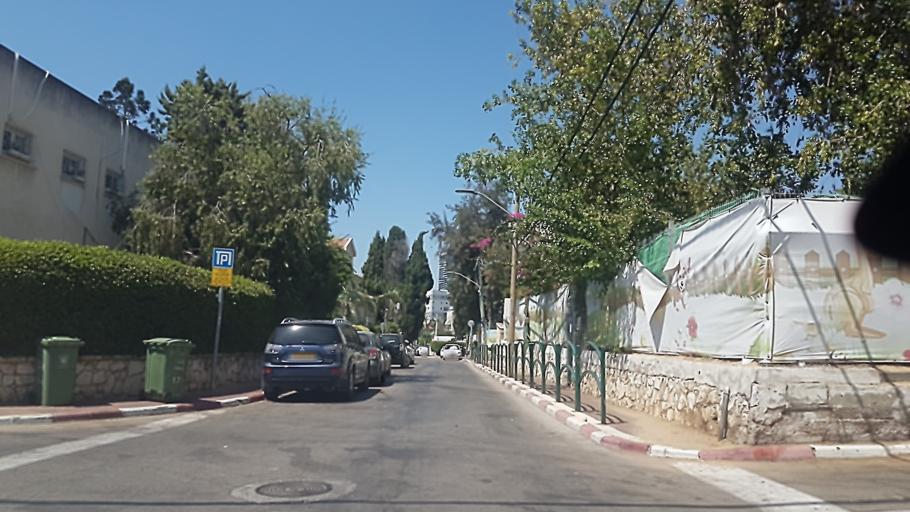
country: IL
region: Tel Aviv
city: Bene Beraq
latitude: 32.0805
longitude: 34.8229
